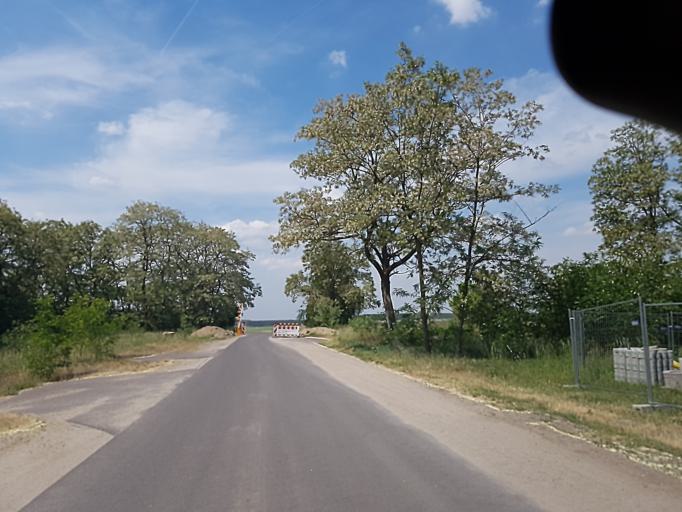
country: DE
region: Brandenburg
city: Gorzke
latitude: 52.1127
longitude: 12.3652
